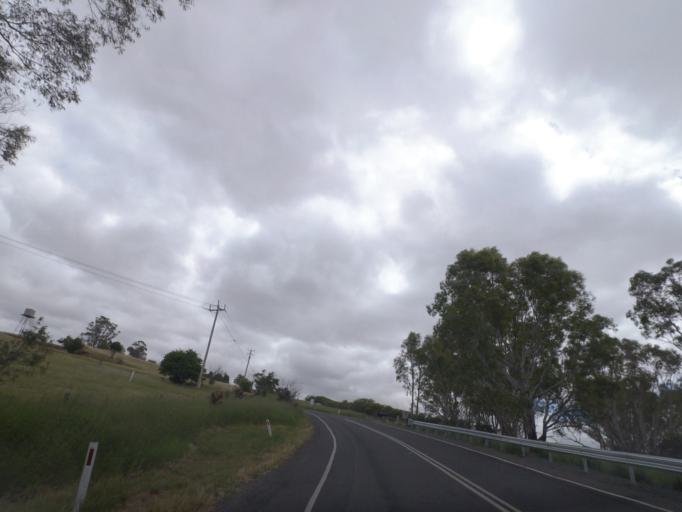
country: AU
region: Victoria
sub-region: Whittlesea
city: Whittlesea
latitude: -37.1894
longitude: 145.0391
